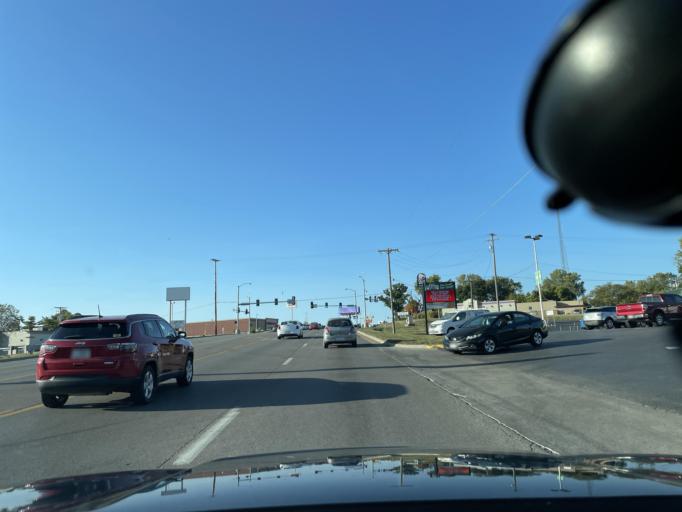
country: US
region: Missouri
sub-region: Andrew County
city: Country Club Village
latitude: 39.7984
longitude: -94.8141
